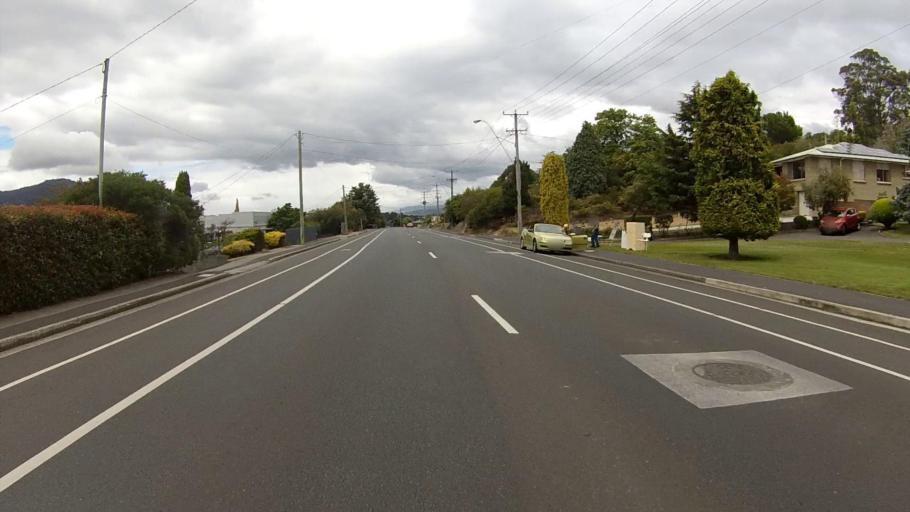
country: AU
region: Tasmania
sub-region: Glenorchy
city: Claremont
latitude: -42.7765
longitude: 147.2508
